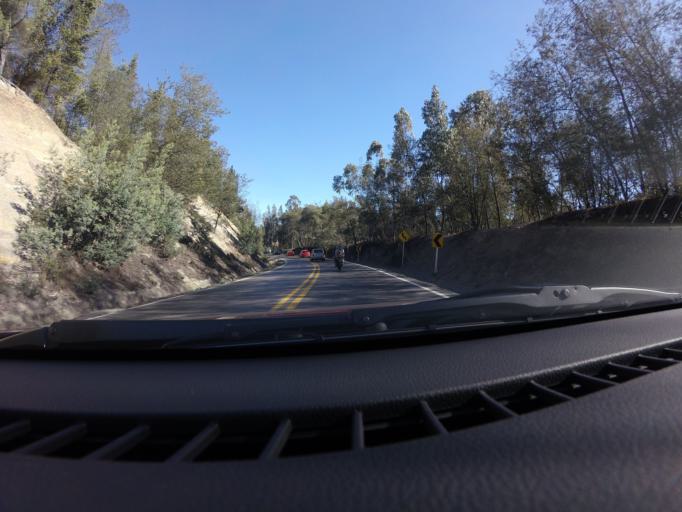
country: CO
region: Cundinamarca
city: Sutatausa
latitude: 5.2438
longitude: -73.8543
